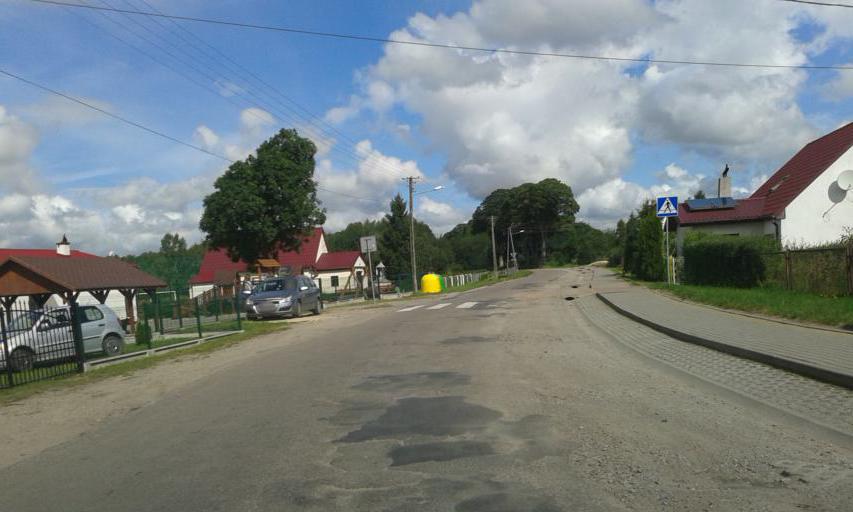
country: PL
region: West Pomeranian Voivodeship
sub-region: Powiat slawienski
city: Slawno
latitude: 54.3052
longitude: 16.6231
